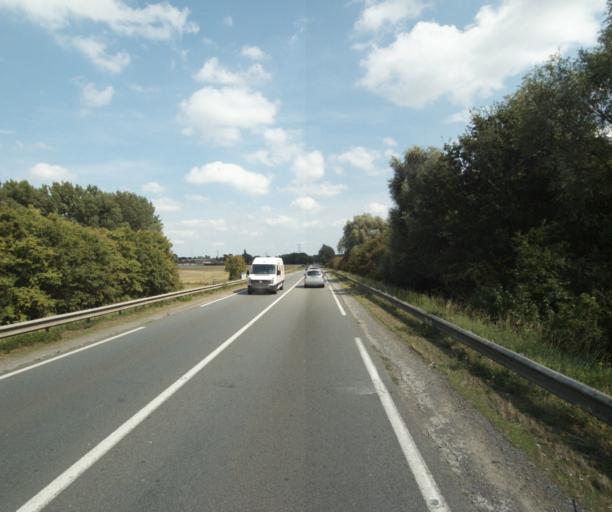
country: FR
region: Nord-Pas-de-Calais
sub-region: Departement du Nord
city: Hem
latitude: 50.6482
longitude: 3.1821
